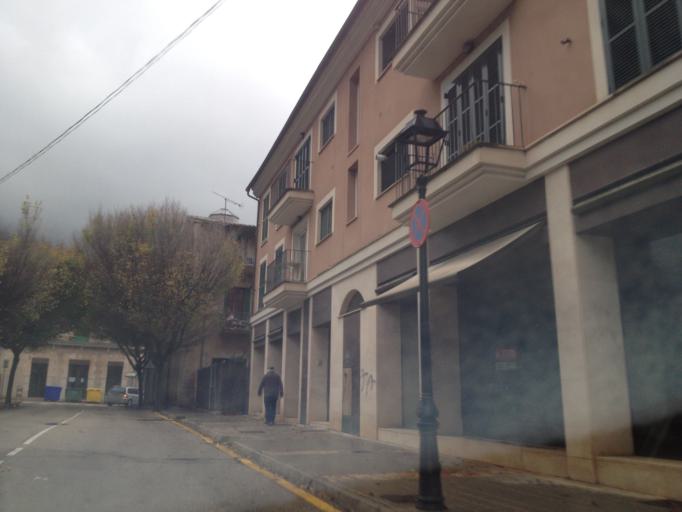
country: ES
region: Balearic Islands
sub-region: Illes Balears
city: Soller
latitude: 39.7688
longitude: 2.7127
